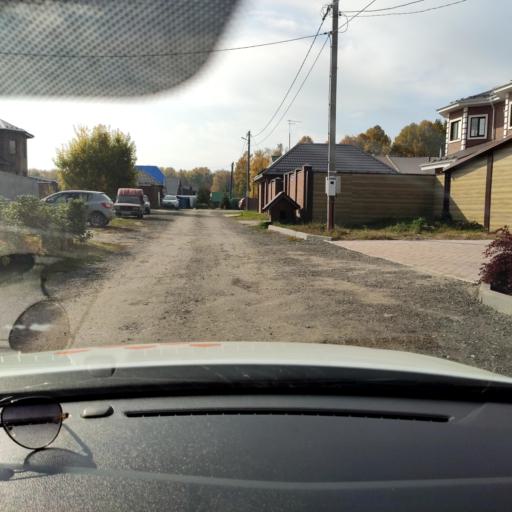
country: RU
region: Tatarstan
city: Stolbishchi
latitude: 55.6799
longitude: 49.1138
